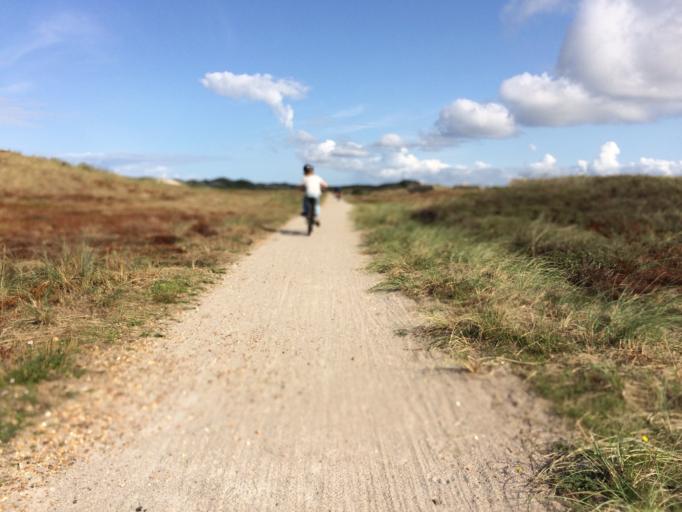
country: DK
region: Central Jutland
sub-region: Ringkobing-Skjern Kommune
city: Hvide Sande
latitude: 55.9044
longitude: 8.1571
